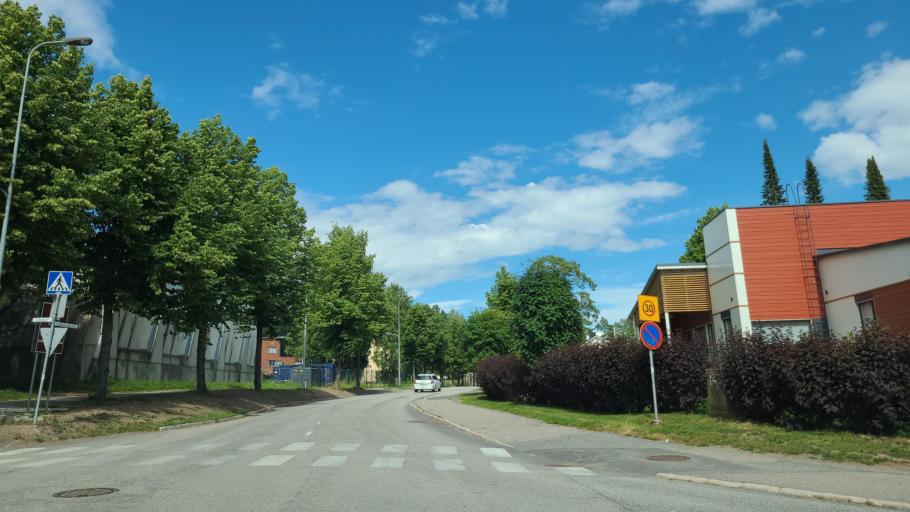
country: FI
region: Central Finland
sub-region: Jyvaeskylae
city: Saeynaetsalo
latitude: 62.2482
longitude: 25.8712
